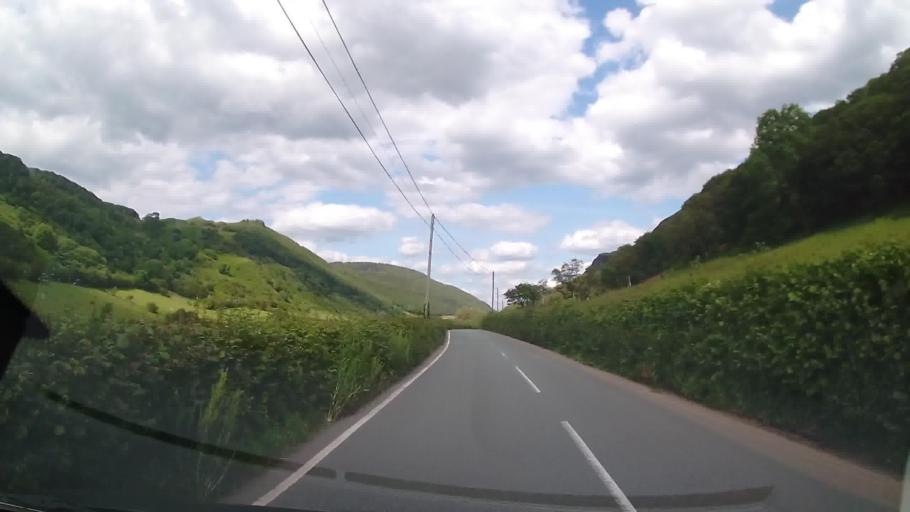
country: GB
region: Wales
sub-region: Gwynedd
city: Tywyn
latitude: 52.6248
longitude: -3.9932
